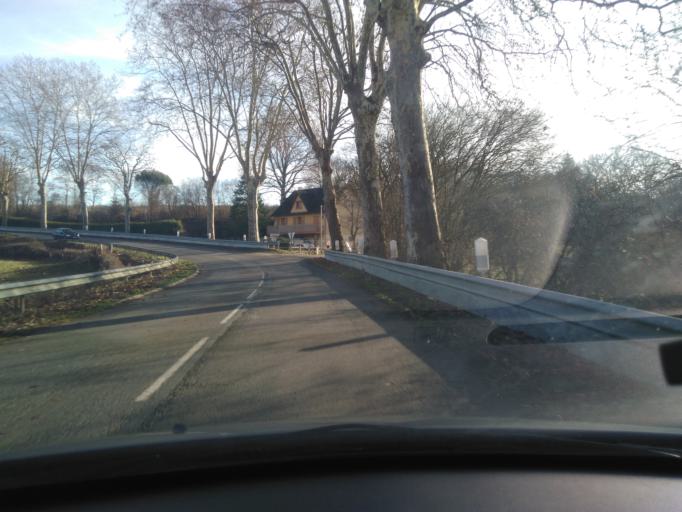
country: FR
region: Centre
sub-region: Departement du Cher
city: Le Chatelet
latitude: 46.6391
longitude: 2.2953
